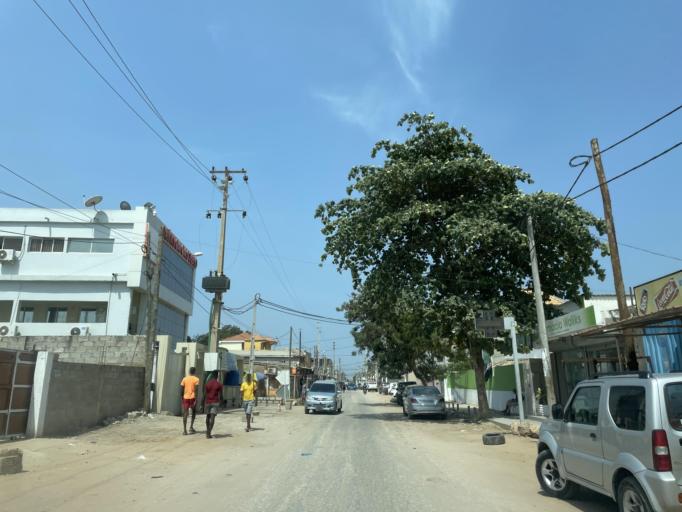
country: AO
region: Luanda
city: Luanda
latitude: -8.8996
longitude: 13.1847
